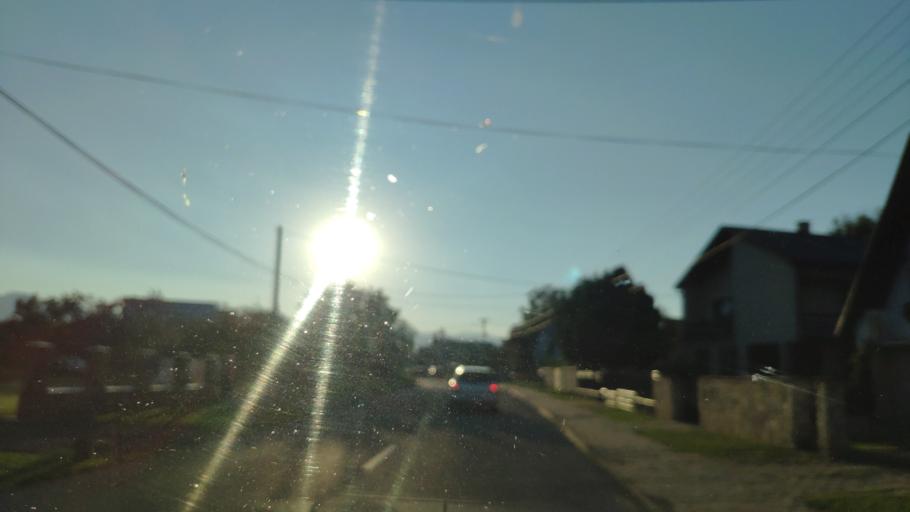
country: SK
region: Presovsky
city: Vranov nad Topl'ou
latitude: 48.8242
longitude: 21.6924
